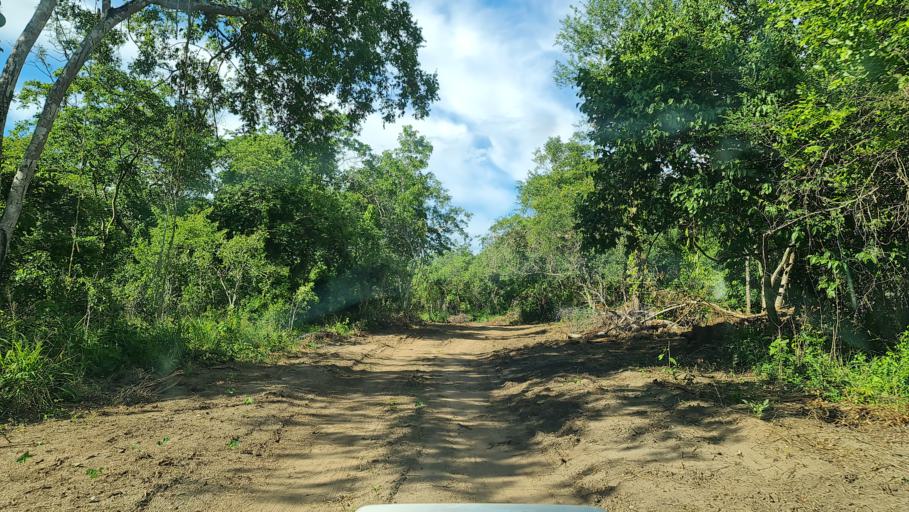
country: MZ
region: Nampula
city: Antonio Enes
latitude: -15.5312
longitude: 40.1259
